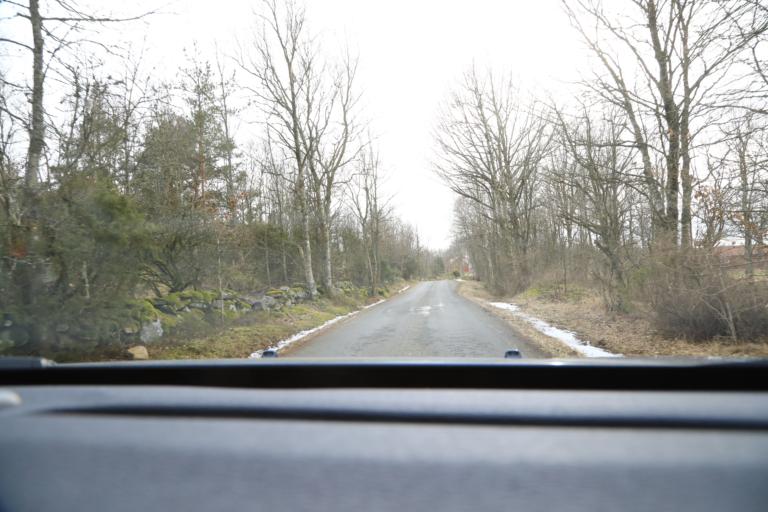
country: SE
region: Halland
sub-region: Varbergs Kommun
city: Veddige
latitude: 57.2160
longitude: 12.2294
